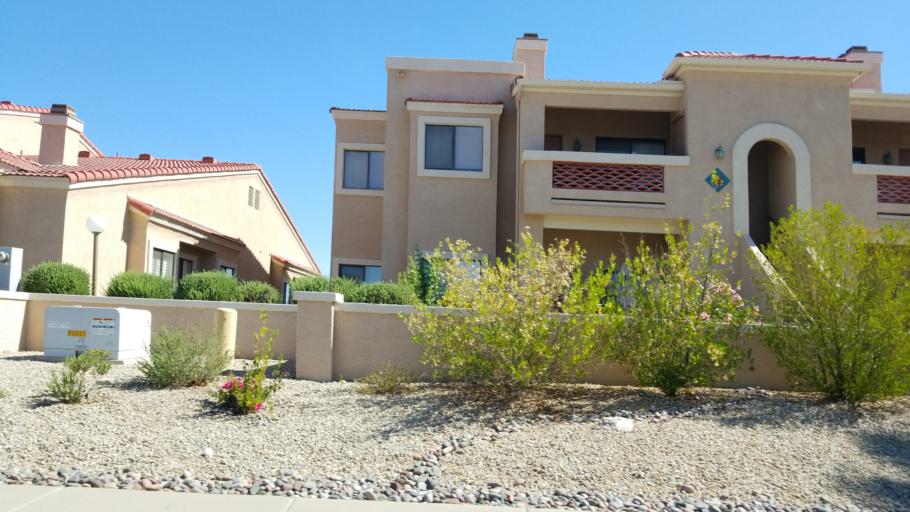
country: US
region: Arizona
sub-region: Maricopa County
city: Fountain Hills
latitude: 33.6107
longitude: -111.7264
